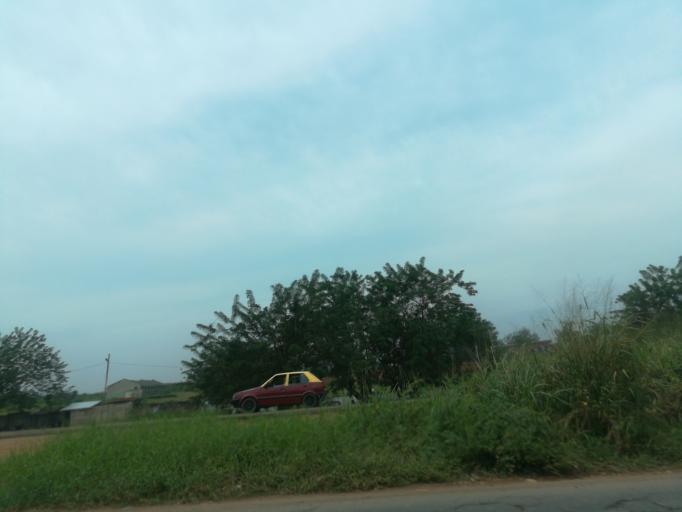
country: NG
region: Oyo
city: Ibadan
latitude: 7.3573
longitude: 3.9236
